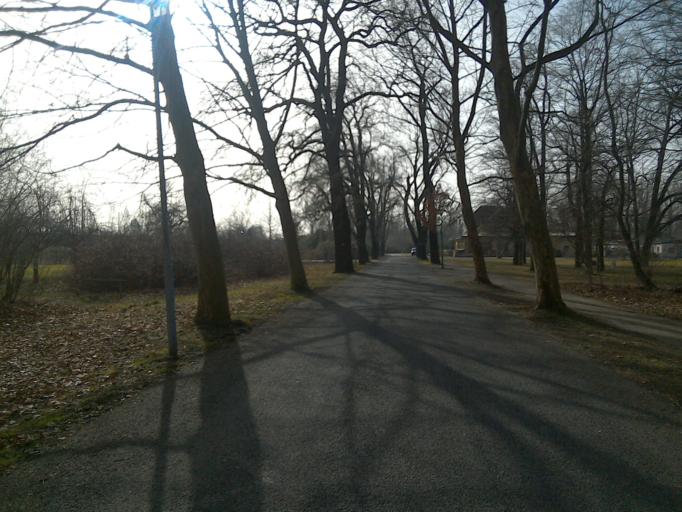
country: DE
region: Saxony
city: Grossenhain
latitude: 51.2919
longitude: 13.5185
